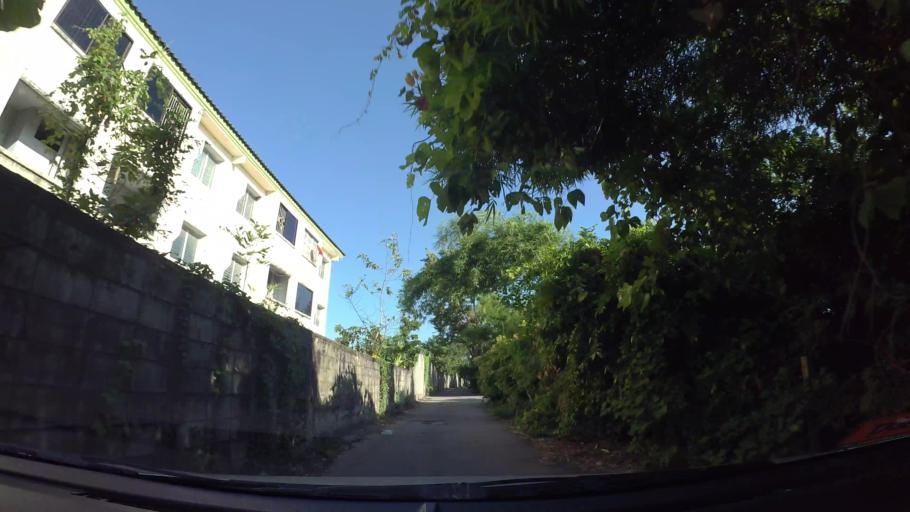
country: TH
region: Chon Buri
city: Si Racha
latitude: 13.1466
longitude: 100.9377
